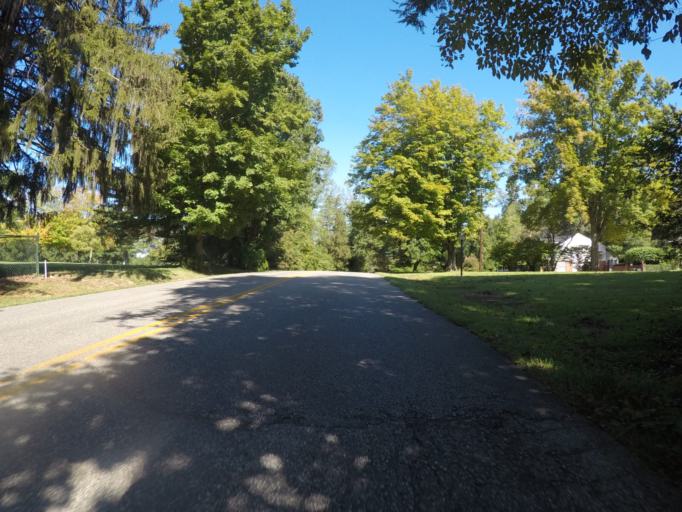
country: US
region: Kentucky
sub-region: Greenup County
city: Russell
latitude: 38.4922
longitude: -82.6937
